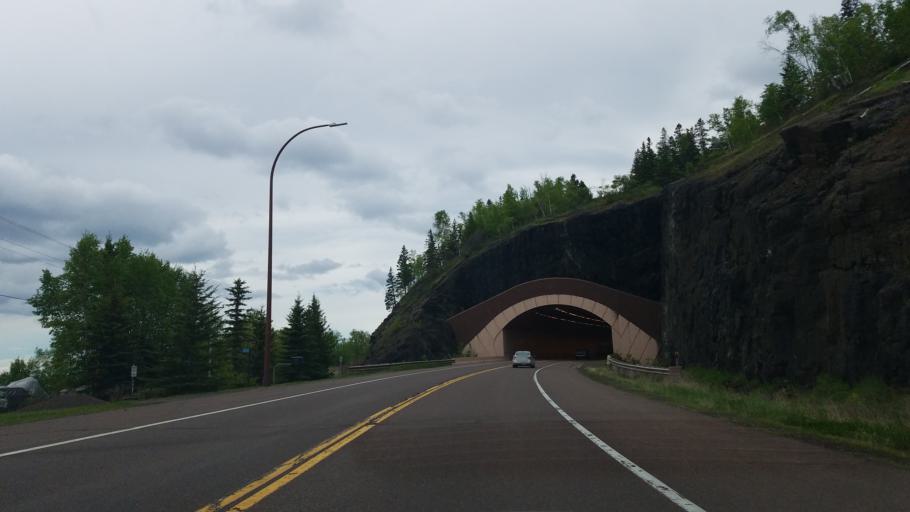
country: US
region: Minnesota
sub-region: Lake County
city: Two Harbors
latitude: 47.0970
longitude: -91.5497
